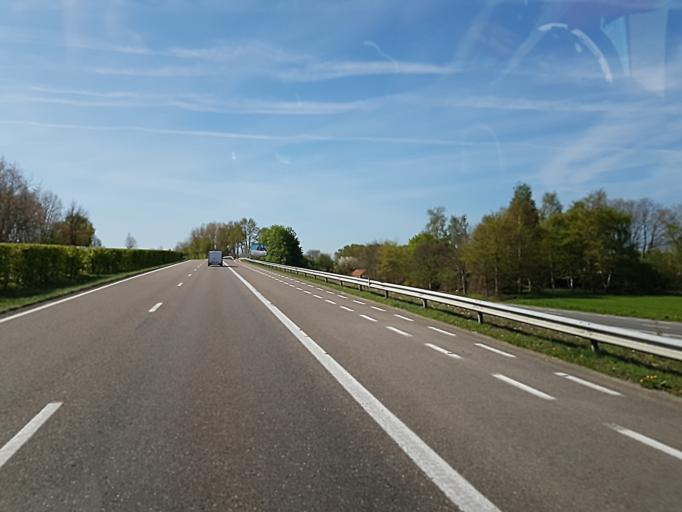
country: BE
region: Flanders
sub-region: Provincie Antwerpen
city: Geel
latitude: 51.1704
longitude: 4.9659
